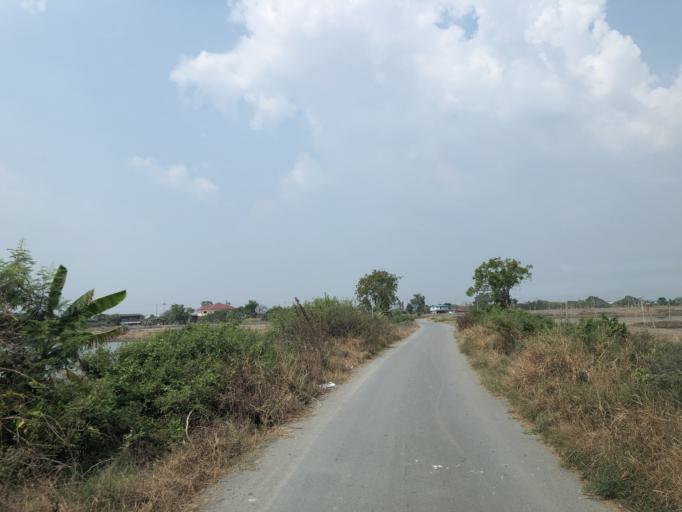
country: TH
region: Samut Prakan
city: Bang Bo
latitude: 13.5459
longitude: 100.8810
